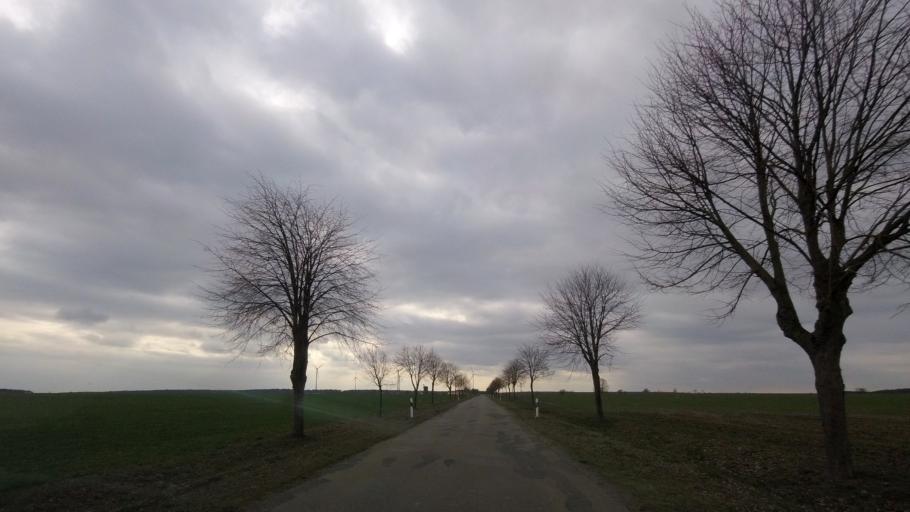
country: DE
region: Saxony-Anhalt
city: Seyda
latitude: 51.9294
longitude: 12.9069
